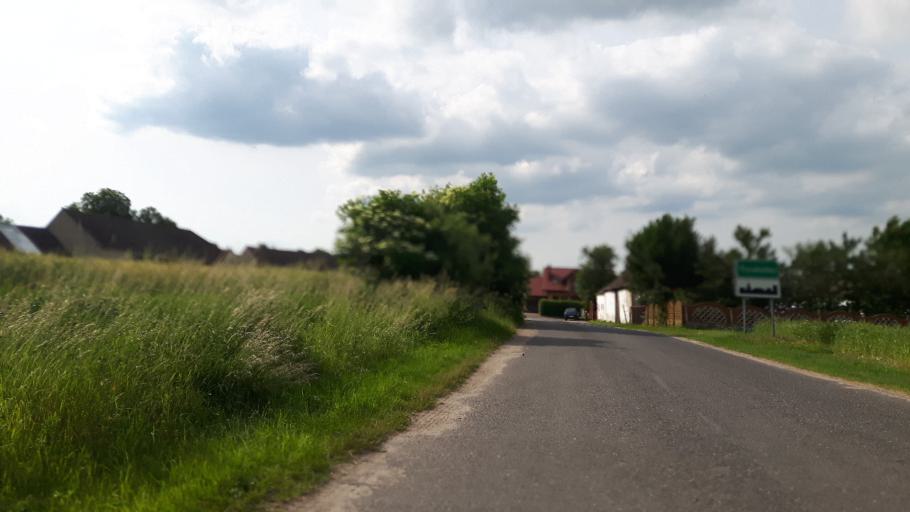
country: PL
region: West Pomeranian Voivodeship
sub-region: Powiat gryficki
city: Gryfice
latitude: 53.8149
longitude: 15.1290
